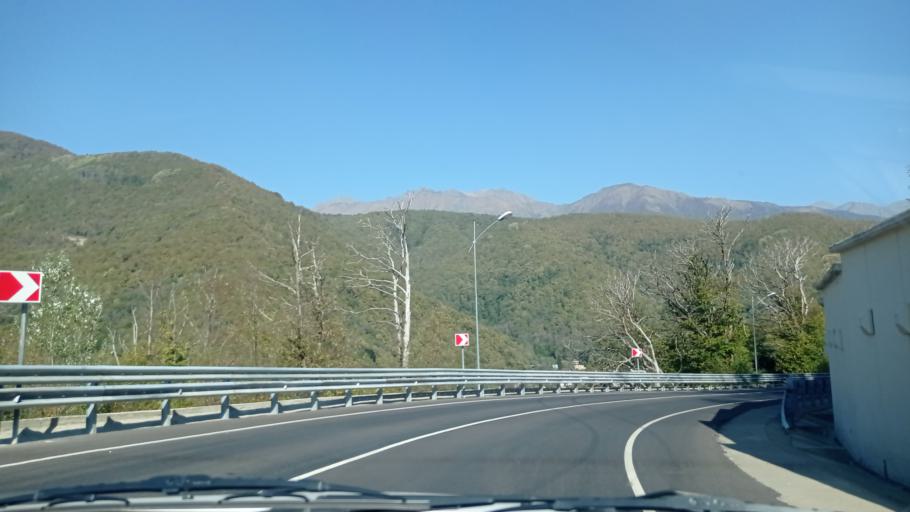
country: RU
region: Krasnodarskiy
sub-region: Sochi City
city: Krasnaya Polyana
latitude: 43.6800
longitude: 40.2425
